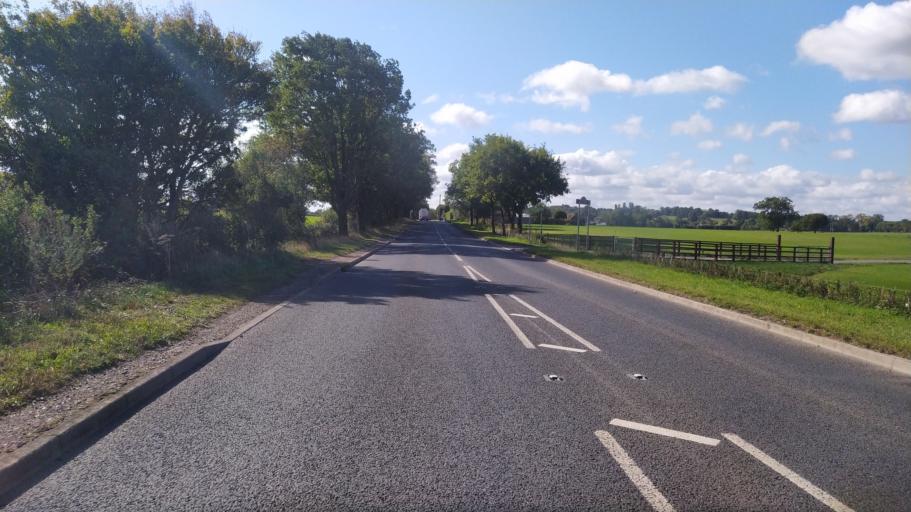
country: GB
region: England
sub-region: West Berkshire
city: Calcot
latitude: 51.4183
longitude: -1.0301
